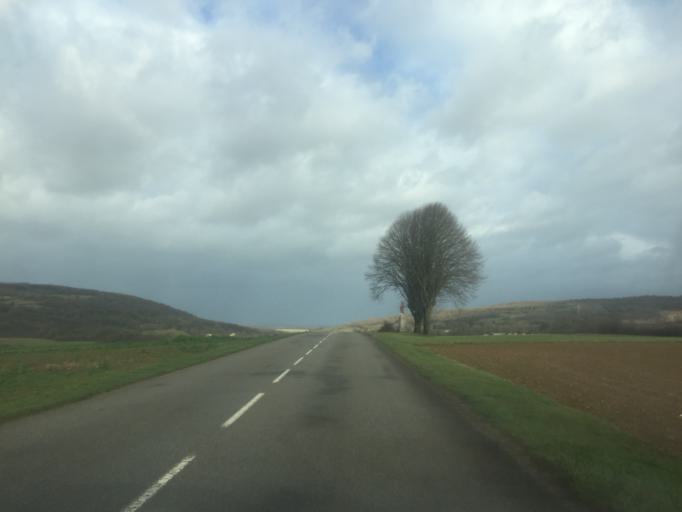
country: FR
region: Franche-Comte
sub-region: Departement du Jura
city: Orchamps
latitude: 47.2108
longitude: 5.6828
